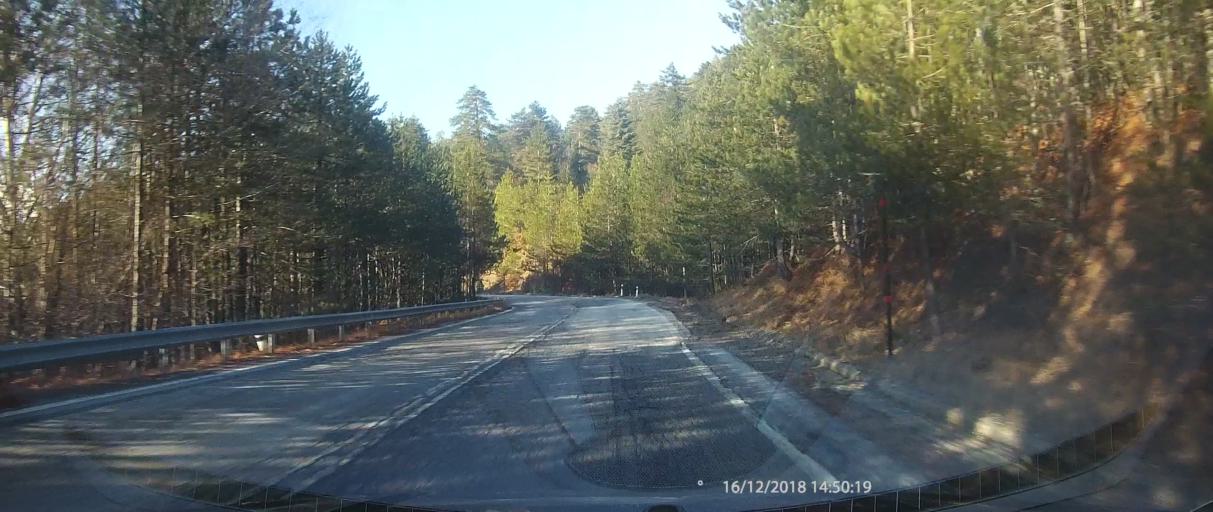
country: GR
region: West Macedonia
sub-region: Nomos Kastorias
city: Nestorio
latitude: 40.2072
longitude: 21.0811
